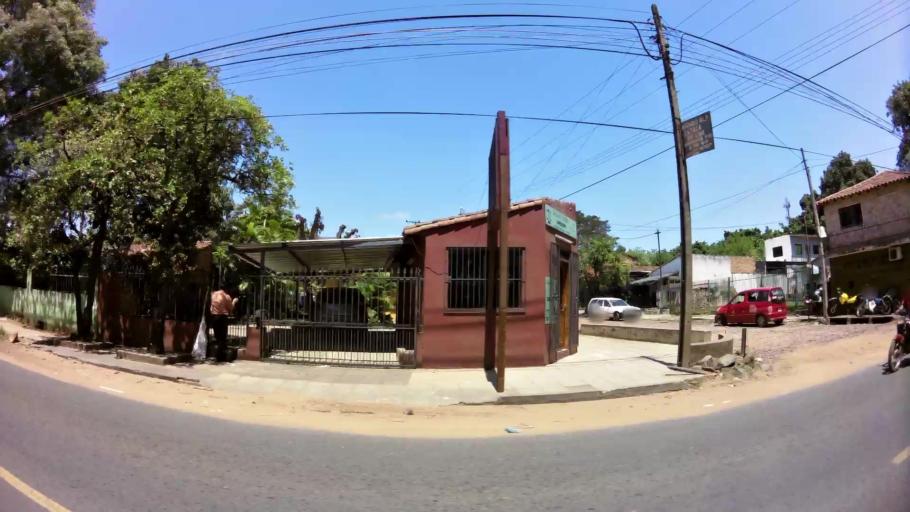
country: PY
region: Central
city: Nemby
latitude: -25.3962
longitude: -57.5393
